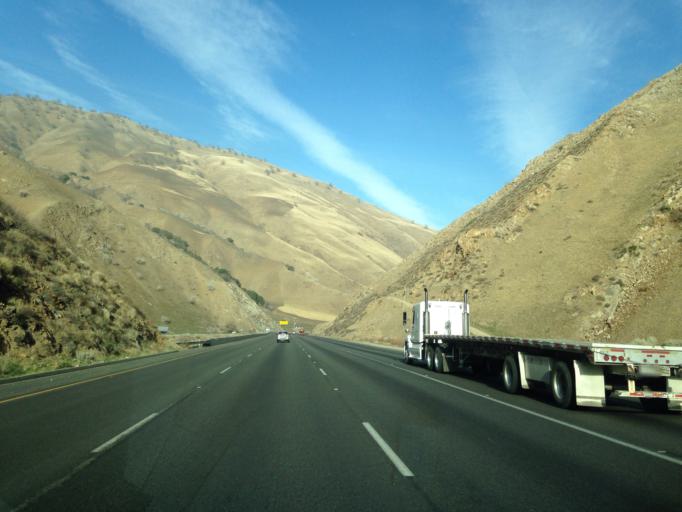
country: US
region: California
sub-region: Kern County
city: Lebec
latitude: 34.8932
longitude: -118.9159
